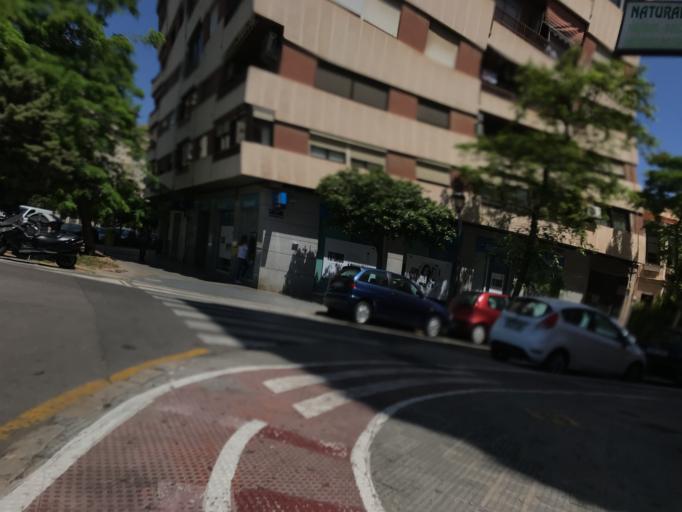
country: ES
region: Valencia
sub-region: Provincia de Valencia
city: Valencia
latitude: 39.4653
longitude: -0.3944
